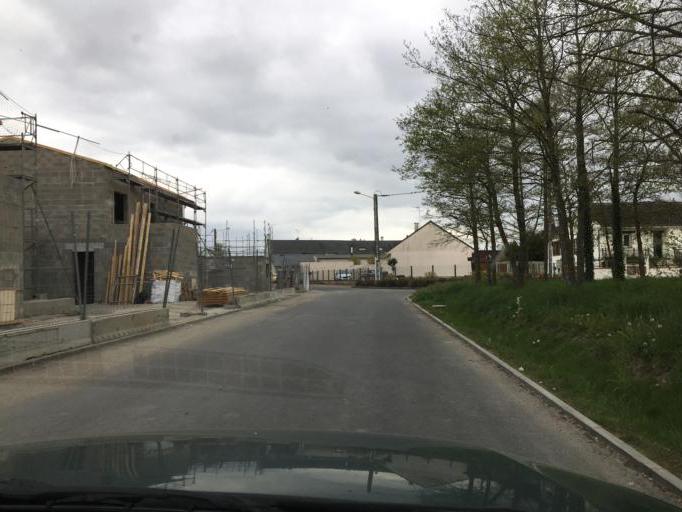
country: FR
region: Centre
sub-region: Departement du Loiret
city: Saint-Jean-de-la-Ruelle
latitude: 47.9224
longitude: 1.8713
